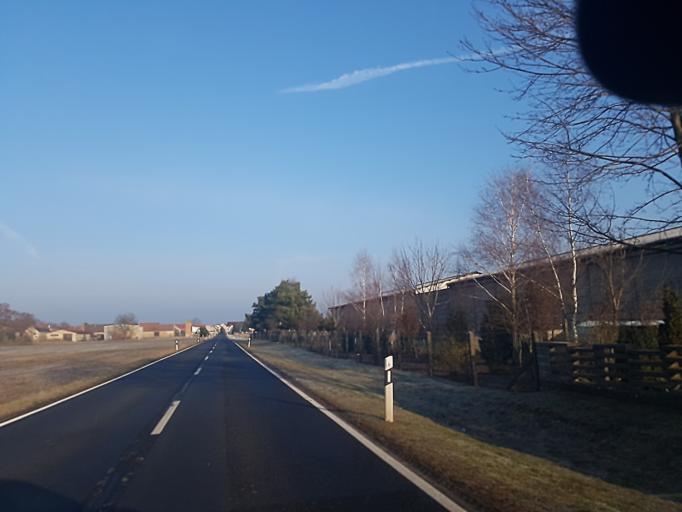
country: DE
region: Brandenburg
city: Golzow
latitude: 52.2426
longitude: 12.6974
